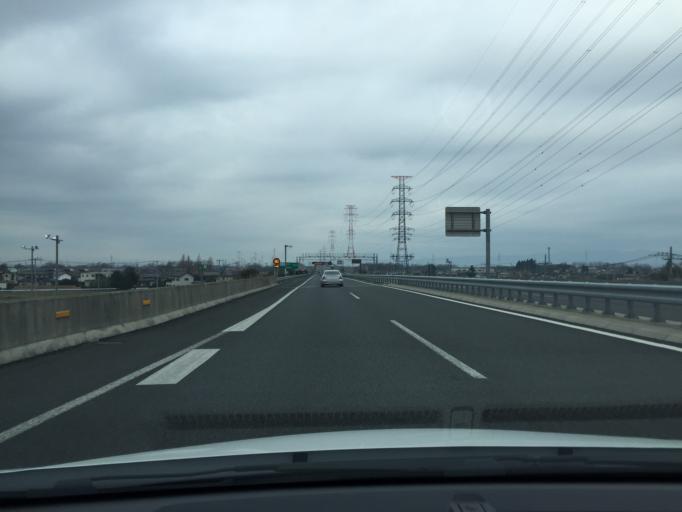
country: JP
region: Saitama
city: Kawagoe
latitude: 35.9806
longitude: 139.4647
